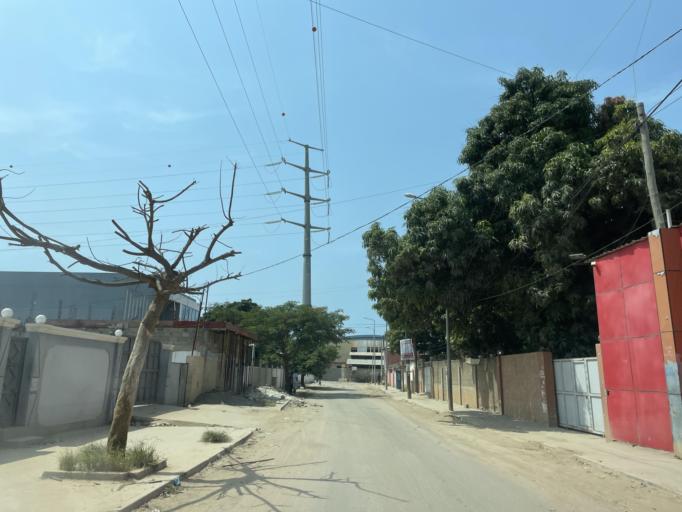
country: AO
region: Luanda
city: Luanda
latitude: -8.9018
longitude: 13.1825
